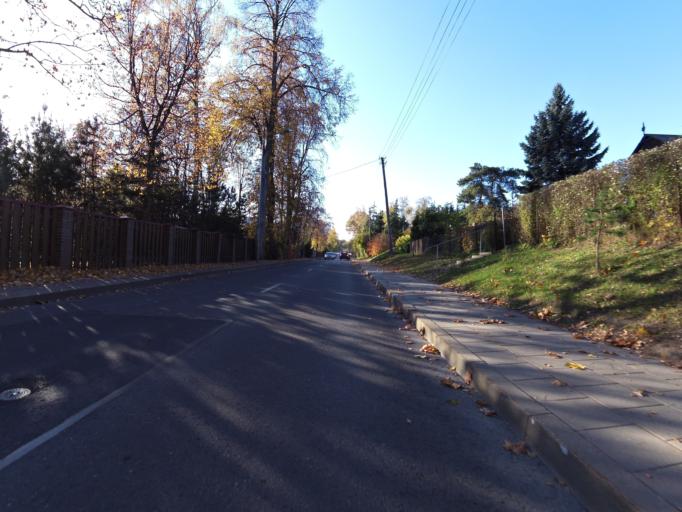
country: LT
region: Vilnius County
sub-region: Vilnius
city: Fabijoniskes
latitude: 54.7456
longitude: 25.2675
